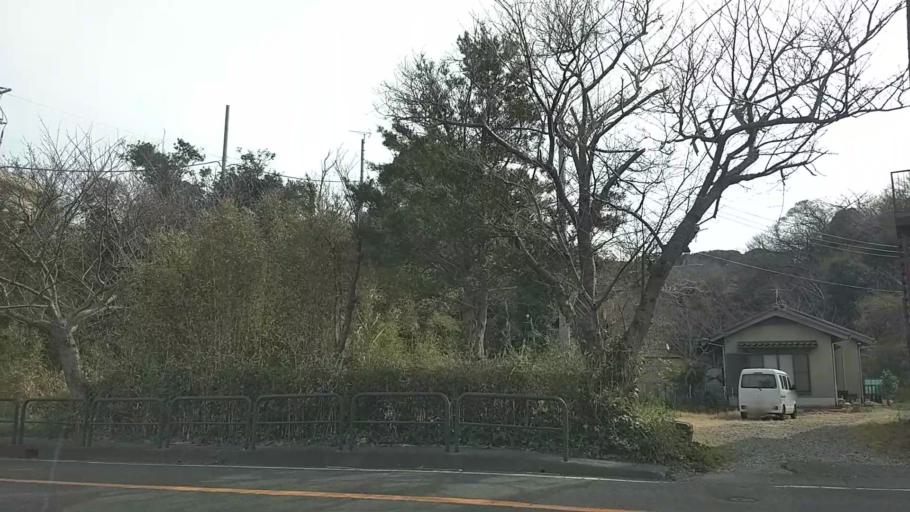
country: JP
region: Shizuoka
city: Shimoda
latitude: 34.6677
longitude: 138.9628
